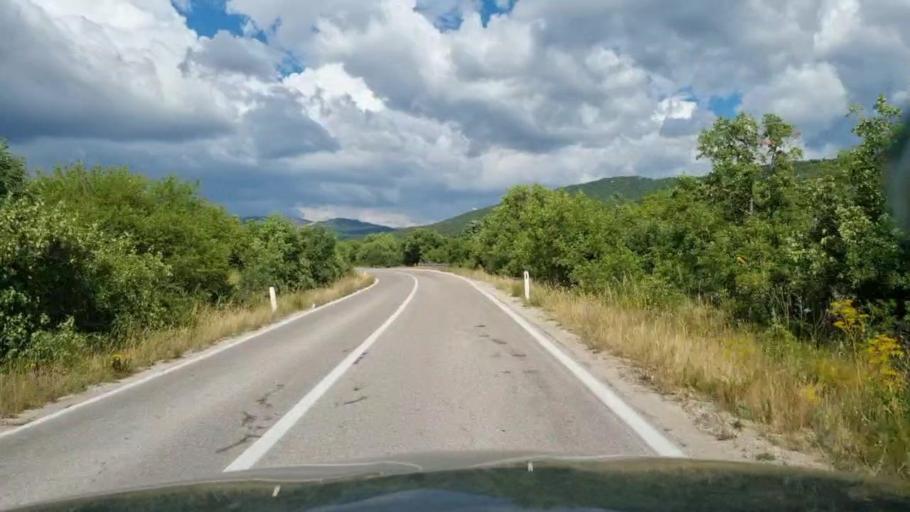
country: BA
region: Federation of Bosnia and Herzegovina
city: Blagaj
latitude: 43.2544
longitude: 17.9914
